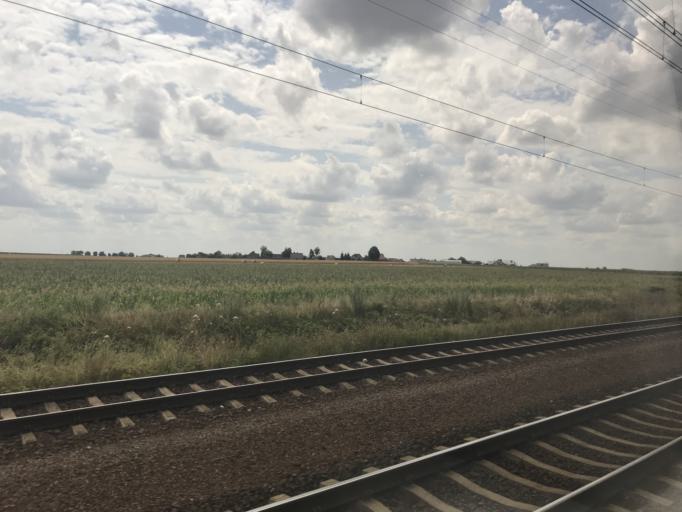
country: PL
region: Greater Poland Voivodeship
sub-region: Powiat poznanski
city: Buk
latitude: 52.3416
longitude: 16.5140
